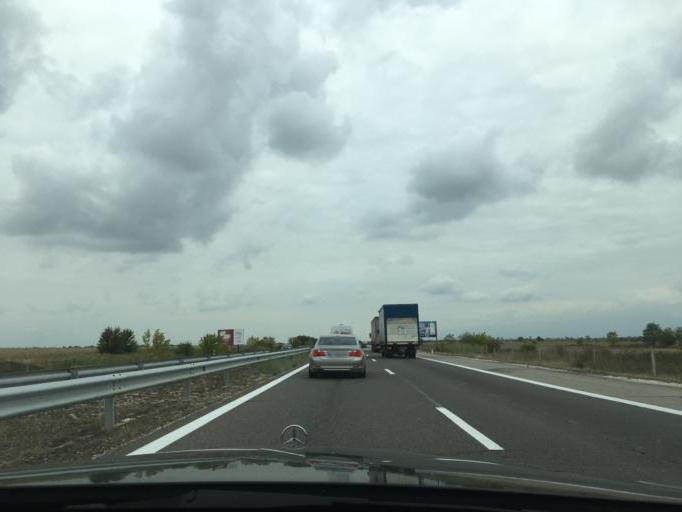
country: BG
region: Pazardzhik
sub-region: Obshtina Pazardzhik
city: Pazardzhik
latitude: 42.2520
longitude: 24.3403
